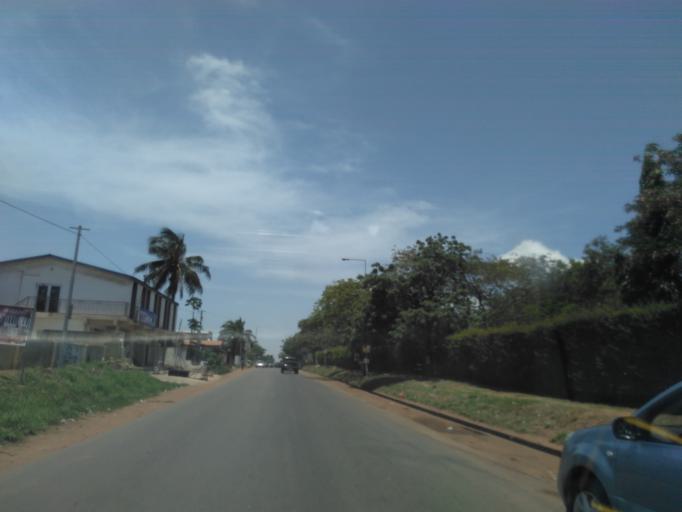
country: GH
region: Greater Accra
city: Tema
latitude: 5.6792
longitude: -0.0225
